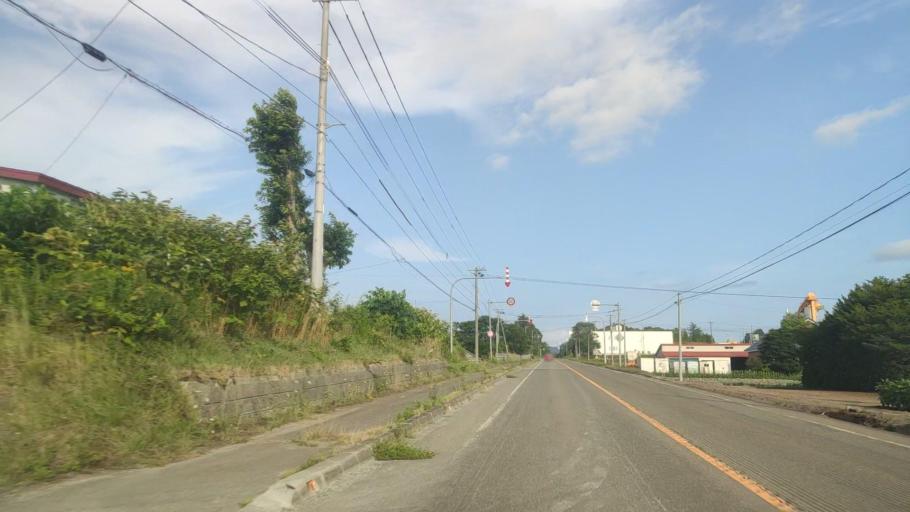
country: JP
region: Hokkaido
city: Iwamizawa
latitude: 43.0260
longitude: 141.8408
